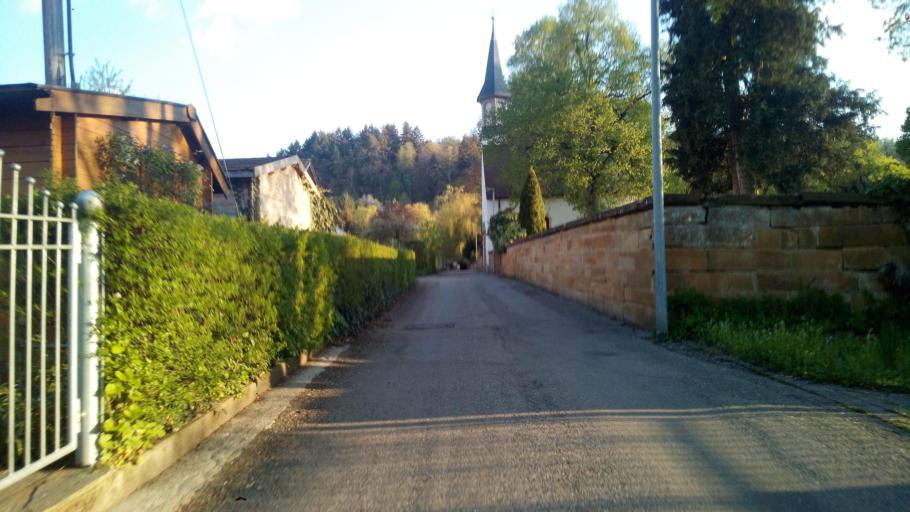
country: DE
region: Baden-Wuerttemberg
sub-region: Regierungsbezirk Stuttgart
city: Donzdorf
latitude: 48.6826
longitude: 9.8142
